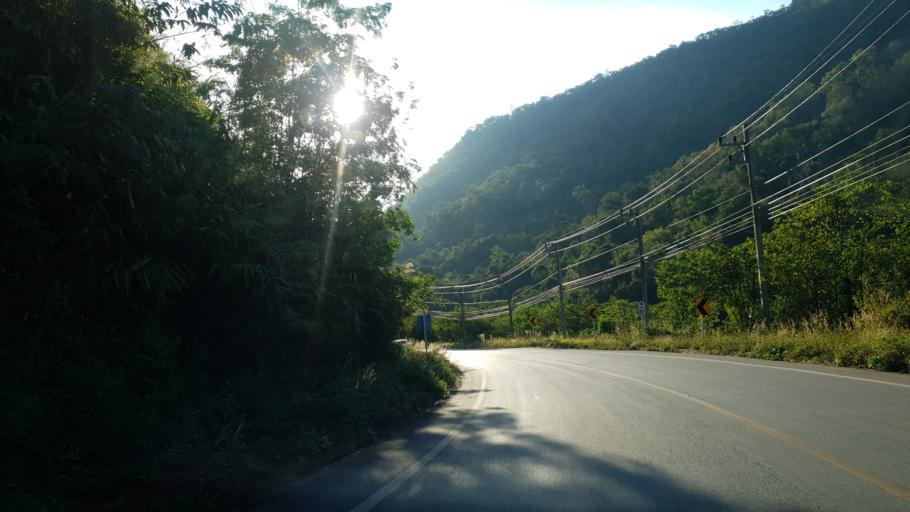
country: TH
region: Loei
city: Dan Sai
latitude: 17.2237
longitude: 101.0284
